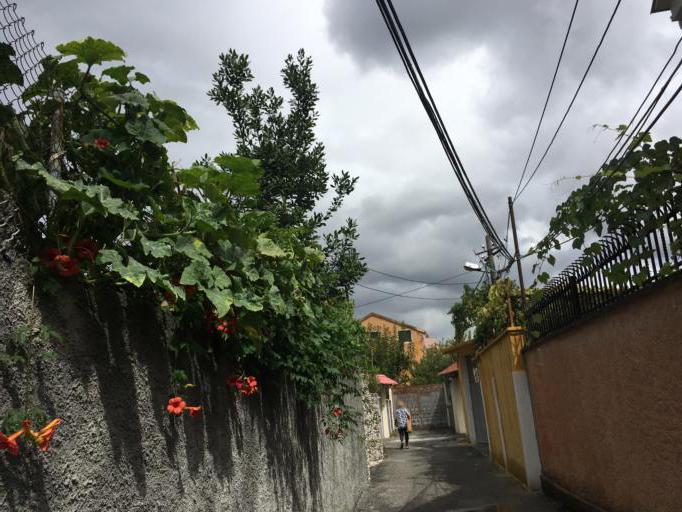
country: AL
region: Shkoder
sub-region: Rrethi i Shkodres
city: Shkoder
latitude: 42.0665
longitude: 19.5226
